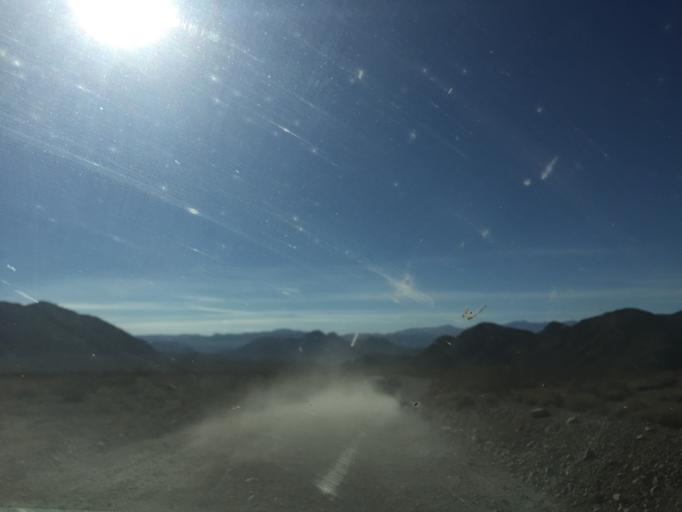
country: US
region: California
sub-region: Inyo County
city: Lone Pine
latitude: 36.7843
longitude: -117.5230
